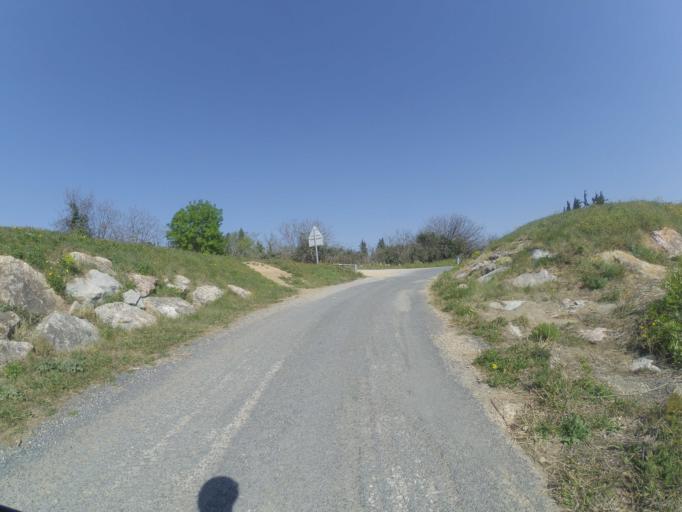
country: FR
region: Languedoc-Roussillon
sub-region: Departement des Pyrenees-Orientales
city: Pezilla-la-Riviere
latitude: 42.6677
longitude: 2.7599
